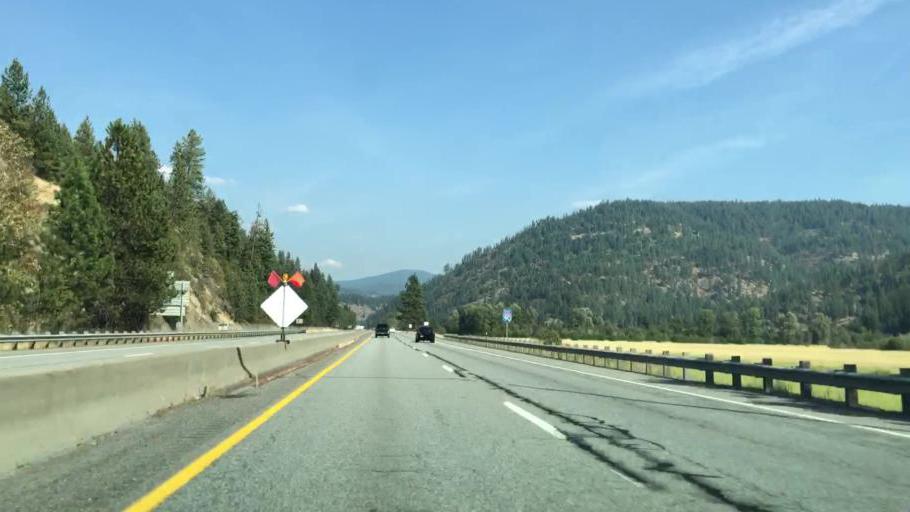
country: US
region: Idaho
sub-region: Kootenai County
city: Coeur d'Alene
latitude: 47.6244
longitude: -116.6435
